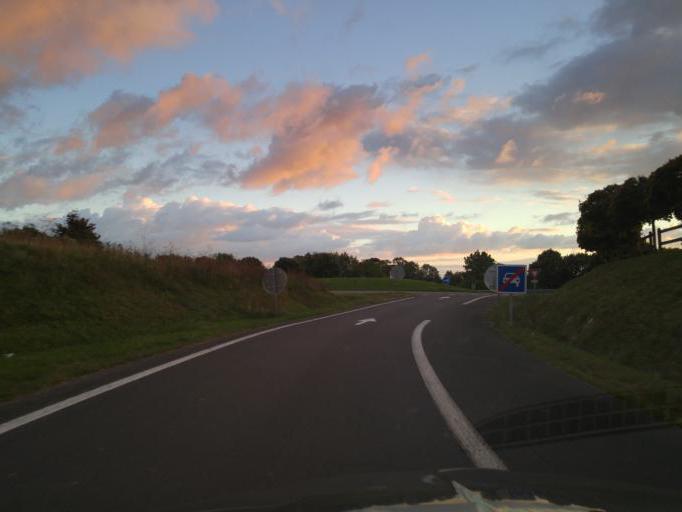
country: FR
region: Lower Normandy
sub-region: Departement du Calvados
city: Grandcamp-Maisy
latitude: 49.3377
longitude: -1.0088
